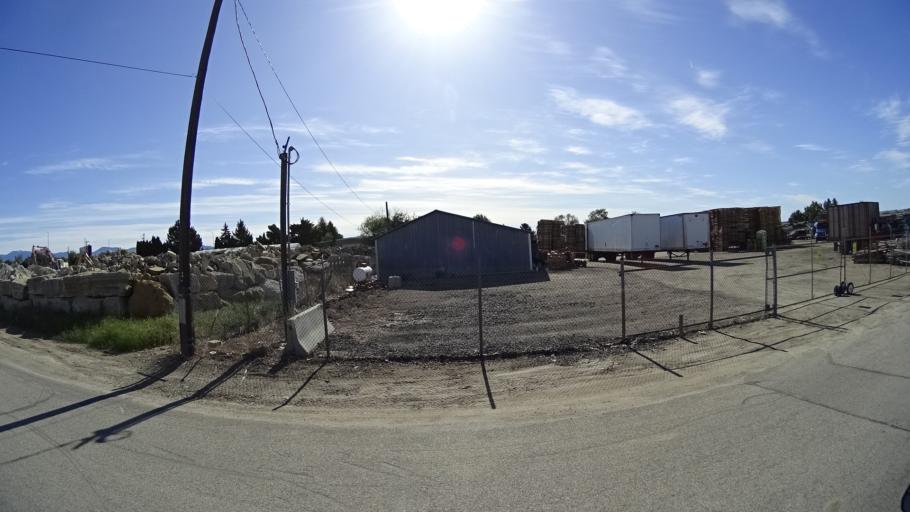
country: US
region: Idaho
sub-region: Ada County
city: Garden City
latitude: 43.5819
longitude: -116.2611
